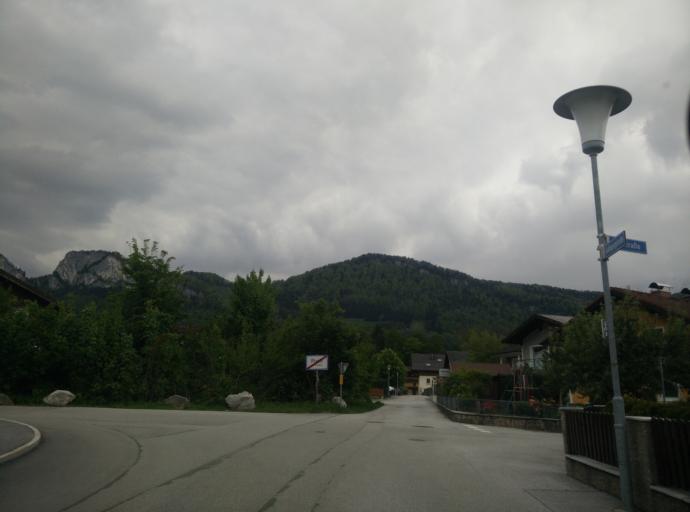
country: AT
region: Salzburg
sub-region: Politischer Bezirk Hallein
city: Puch bei Hallein
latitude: 47.7064
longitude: 13.0864
